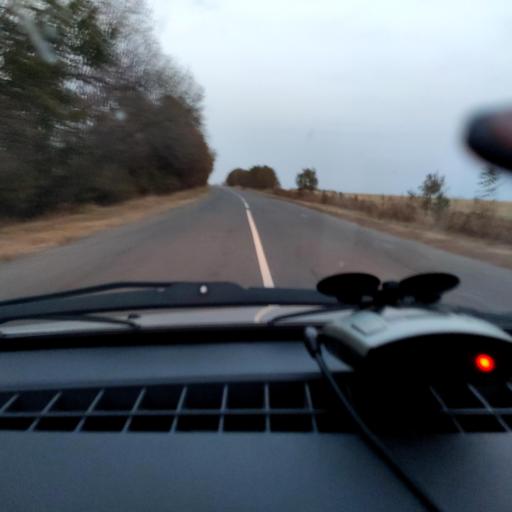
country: RU
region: Voronezj
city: Uryv-Pokrovka
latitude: 51.2411
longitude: 38.9842
